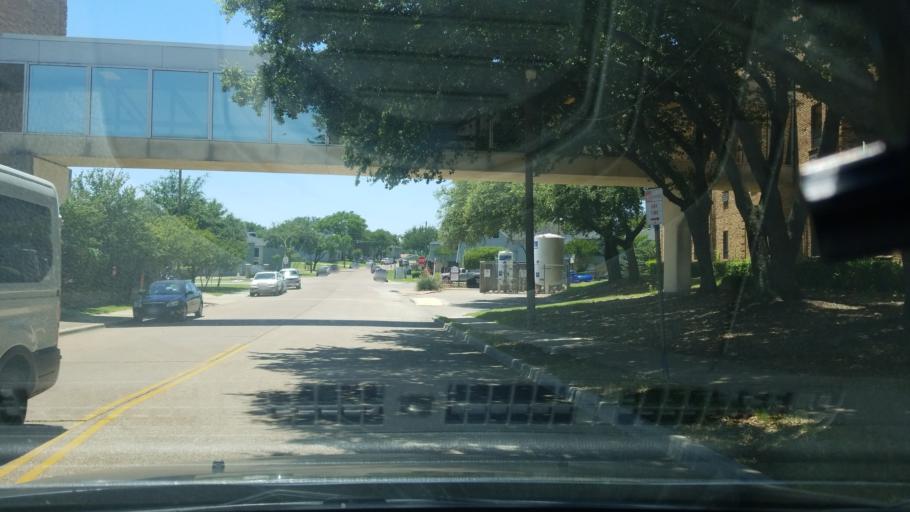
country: US
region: Texas
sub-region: Dallas County
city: Mesquite
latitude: 32.7774
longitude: -96.6001
